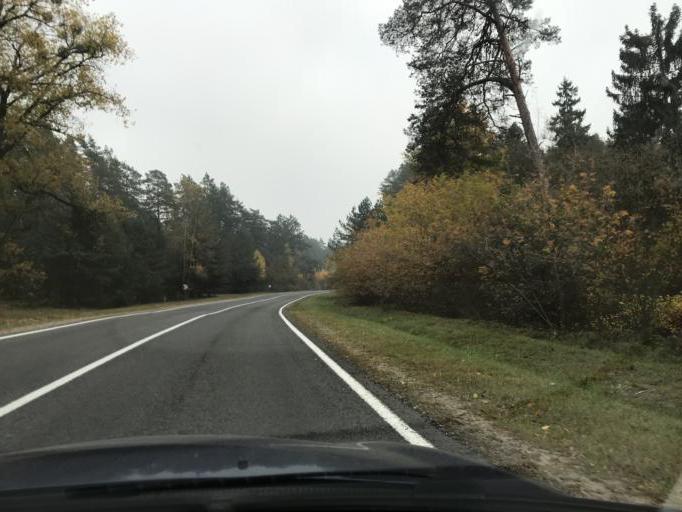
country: BY
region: Grodnenskaya
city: Hrodna
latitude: 53.8437
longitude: 23.8937
